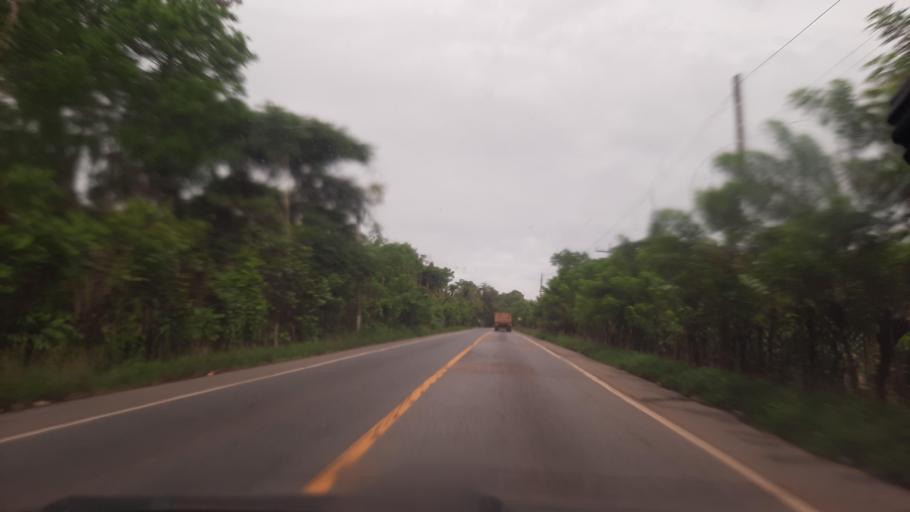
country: GT
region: Izabal
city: Morales
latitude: 15.5234
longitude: -88.7853
